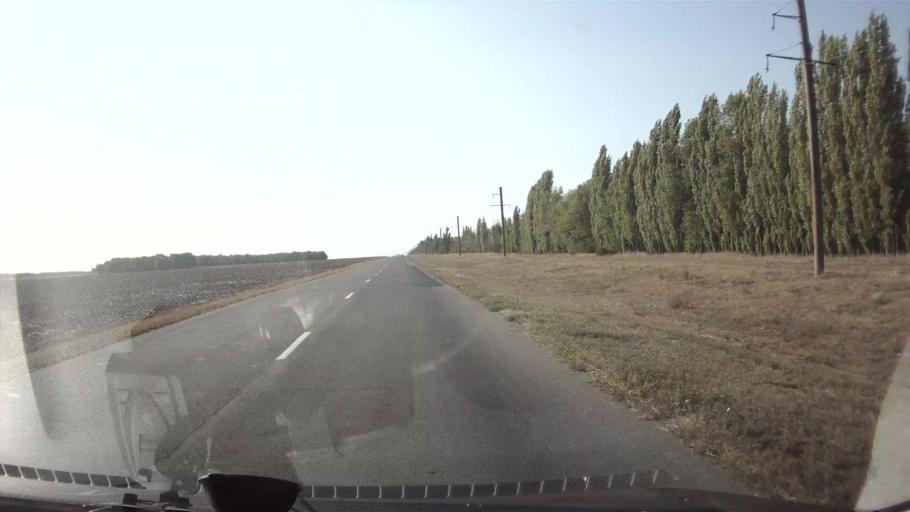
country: RU
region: Rostov
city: Tselina
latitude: 46.5330
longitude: 40.8998
